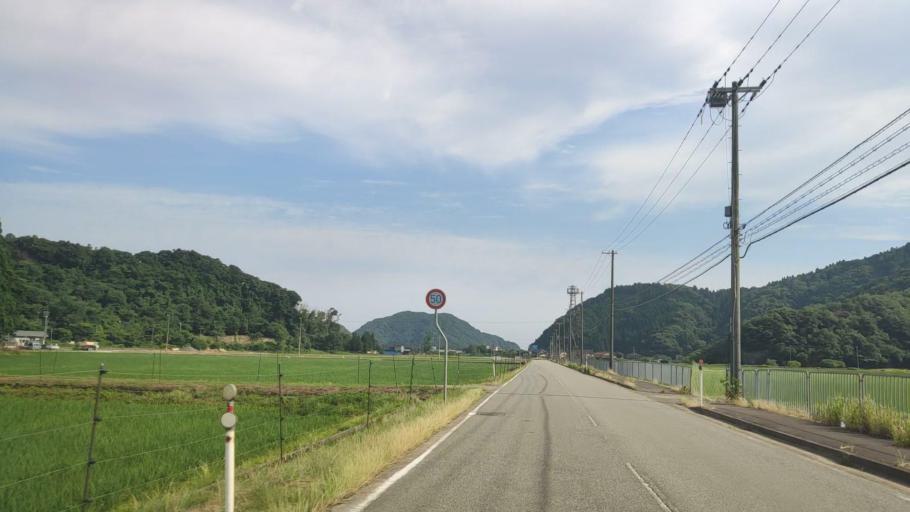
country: JP
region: Hyogo
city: Toyooka
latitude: 35.6288
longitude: 134.8410
